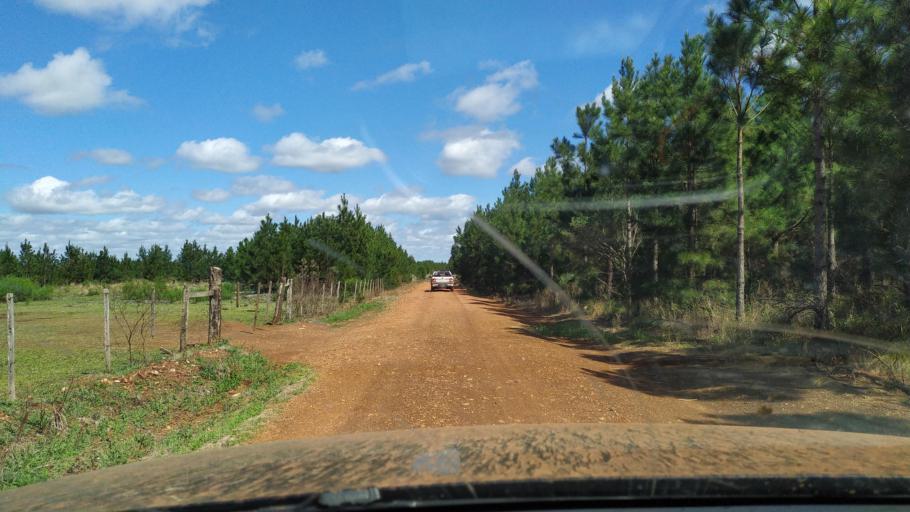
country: AR
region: Corrientes
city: Santo Tome
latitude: -28.4636
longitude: -55.9748
